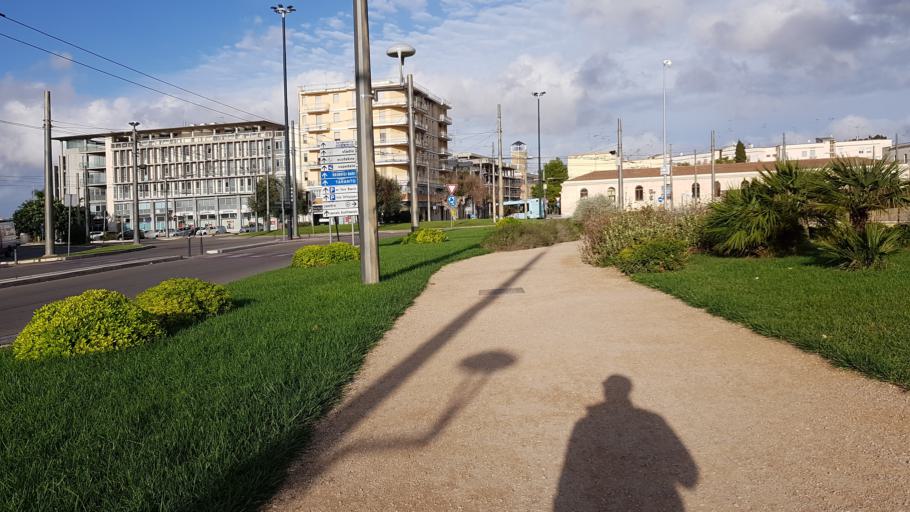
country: IT
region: Apulia
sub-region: Provincia di Lecce
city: Lecce
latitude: 40.3602
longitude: 18.1696
